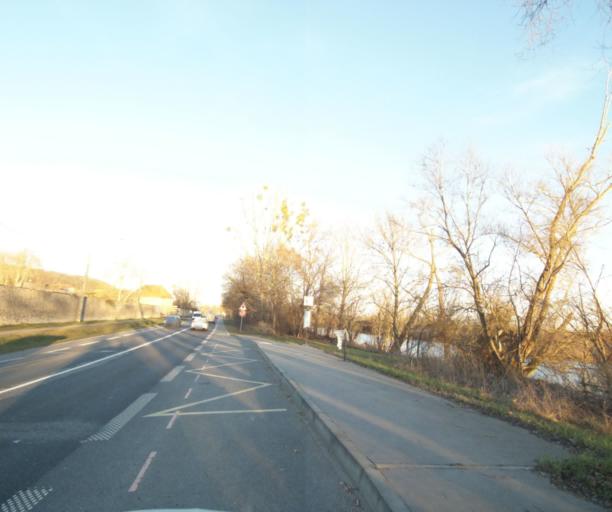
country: FR
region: Lorraine
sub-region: Departement de Meurthe-et-Moselle
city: Laneuveville-devant-Nancy
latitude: 48.6615
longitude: 6.2411
